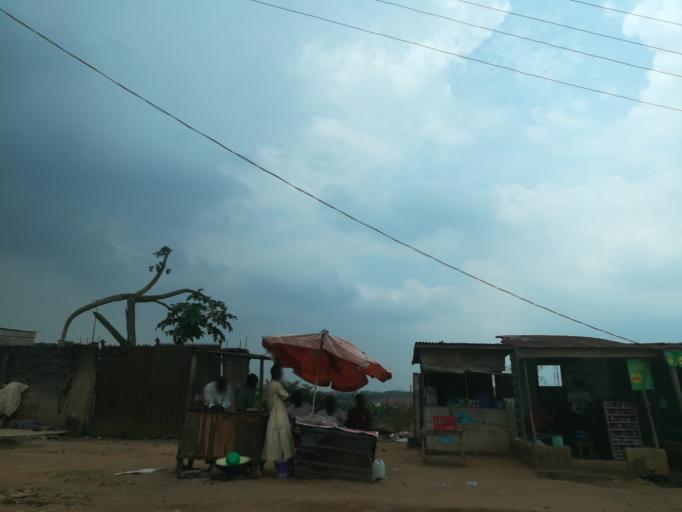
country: NG
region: Lagos
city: Ikorodu
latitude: 6.6051
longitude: 3.5863
